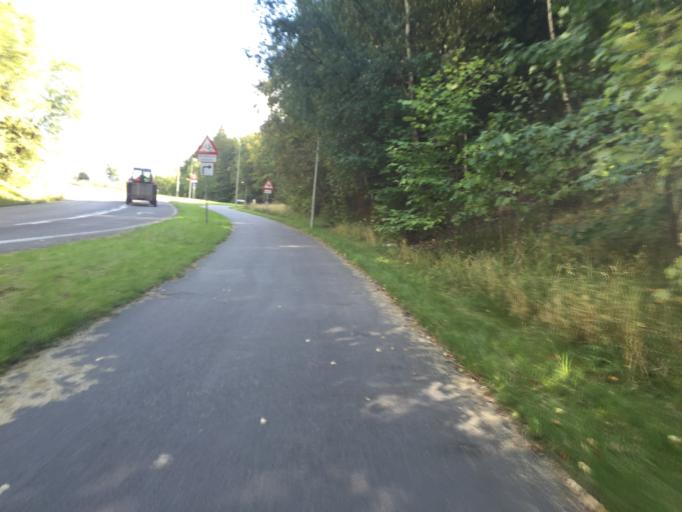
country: DK
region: Capital Region
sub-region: Herlev Kommune
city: Herlev
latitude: 55.7669
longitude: 12.4291
